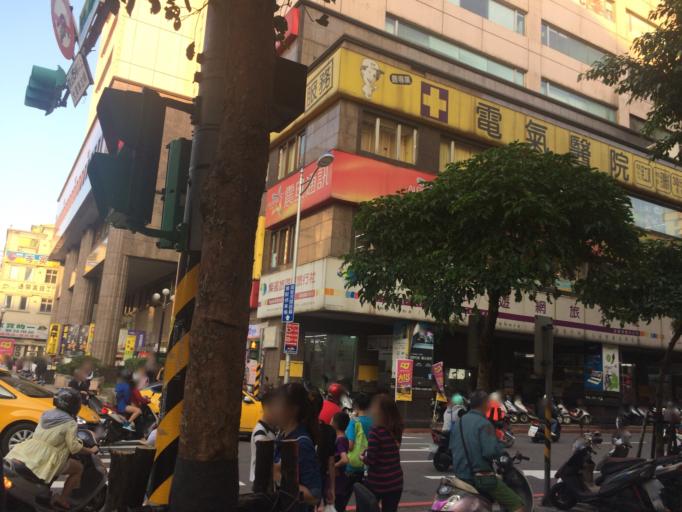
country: TW
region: Taiwan
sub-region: Keelung
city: Keelung
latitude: 25.1317
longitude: 121.7449
